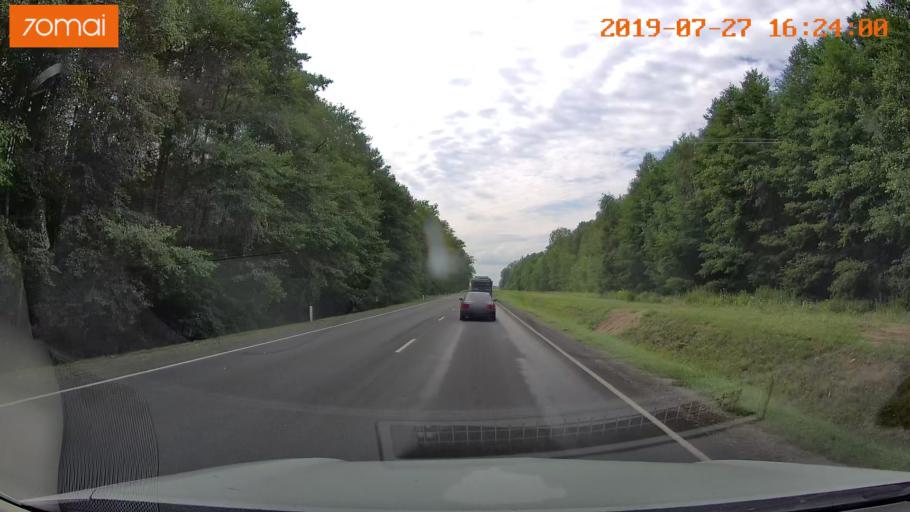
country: RU
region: Kaliningrad
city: Zheleznodorozhnyy
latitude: 54.6328
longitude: 21.4614
